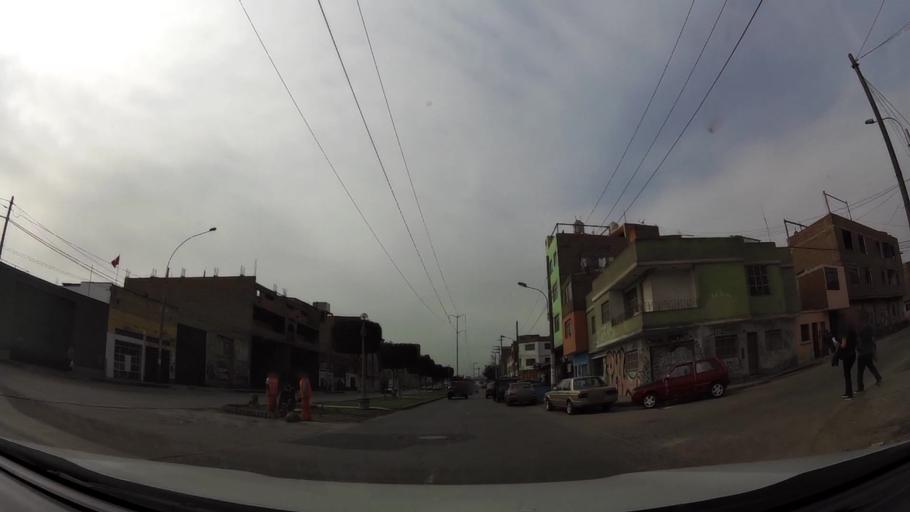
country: PE
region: Callao
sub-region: Callao
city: Callao
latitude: -12.0331
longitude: -77.0959
